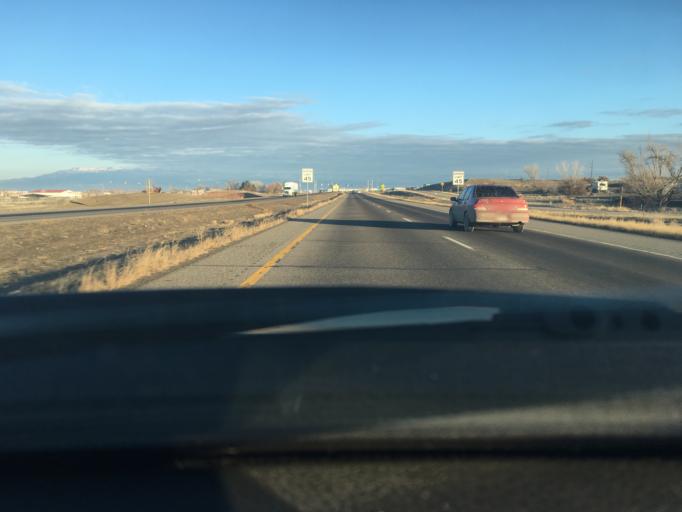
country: US
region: Colorado
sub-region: Montrose County
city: Olathe
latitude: 38.6010
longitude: -107.9731
